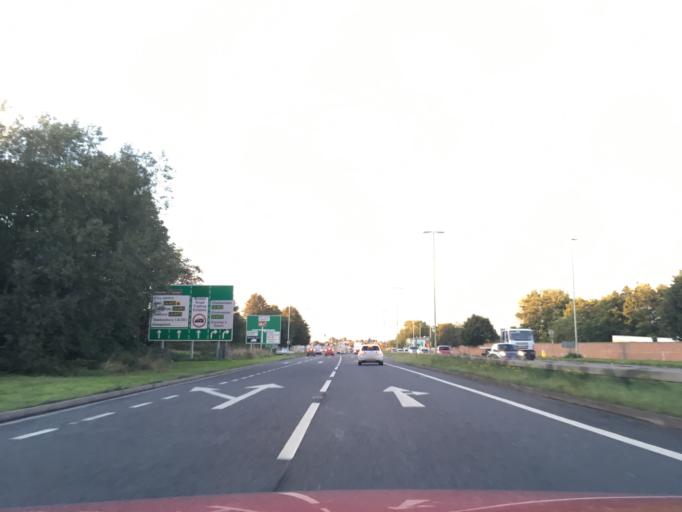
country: GB
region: England
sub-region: Gloucestershire
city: Gloucester
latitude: 51.8338
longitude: -2.2720
